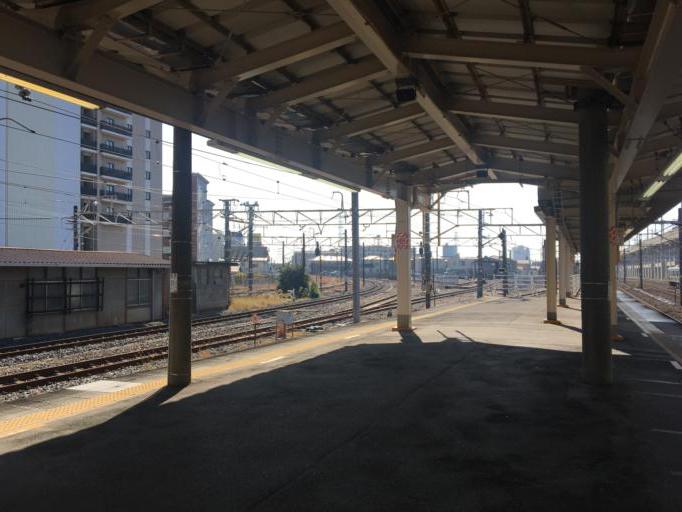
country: JP
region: Tochigi
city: Oyama
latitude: 36.3115
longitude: 139.8058
